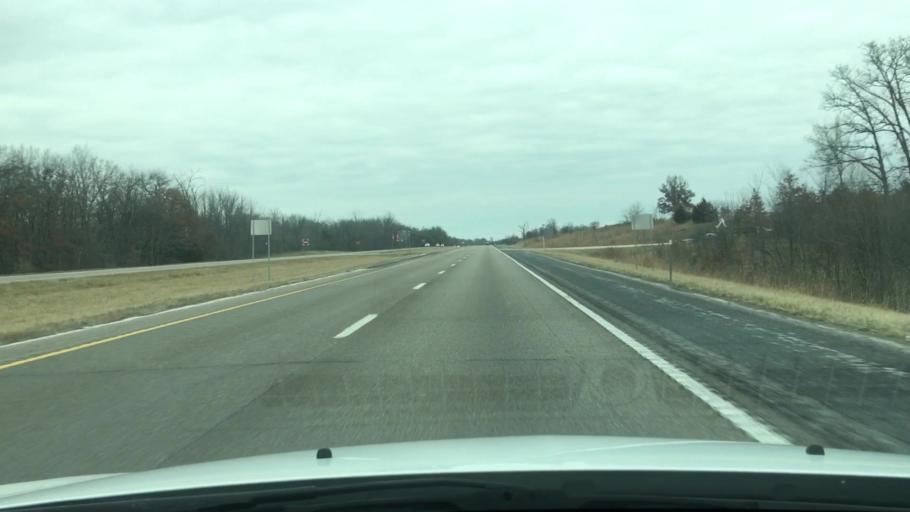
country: US
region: Missouri
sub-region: Callaway County
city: Fulton
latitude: 38.9876
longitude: -91.8938
